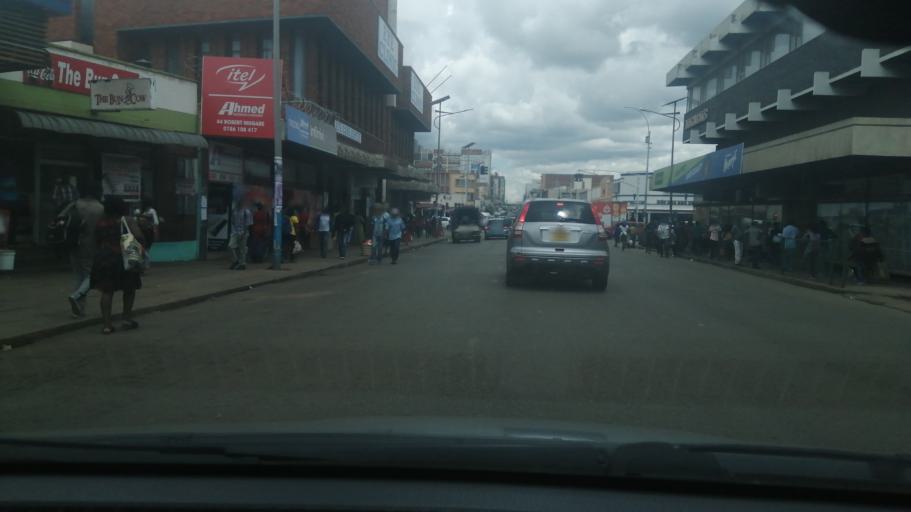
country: ZW
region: Harare
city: Harare
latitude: -17.8338
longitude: 31.0445
